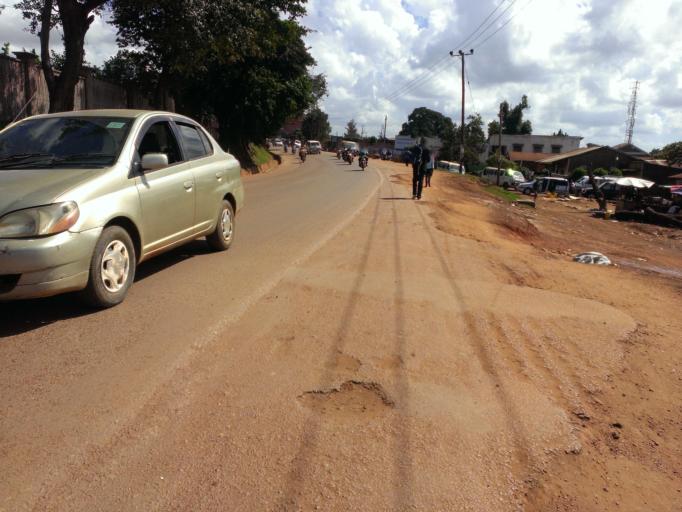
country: UG
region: Central Region
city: Kampala Central Division
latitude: 0.3293
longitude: 32.5578
